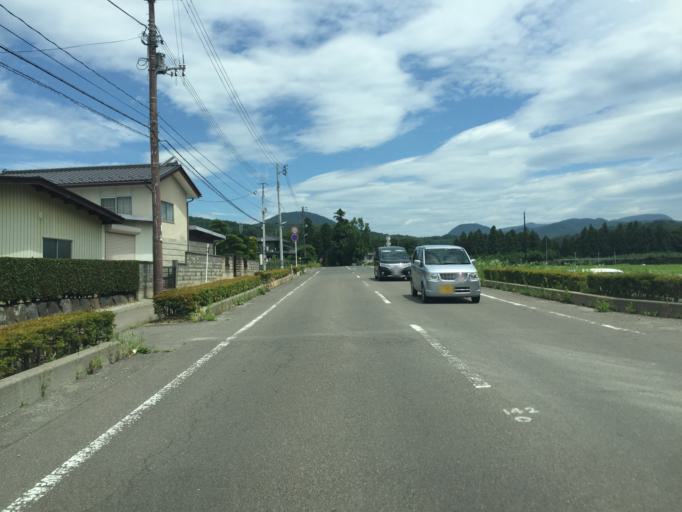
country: JP
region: Fukushima
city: Fukushima-shi
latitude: 37.8183
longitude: 140.4156
